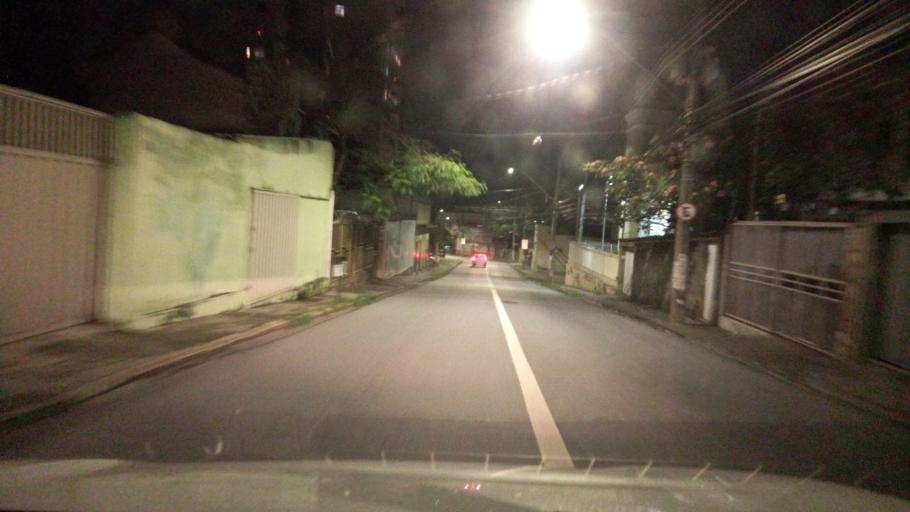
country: BR
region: Minas Gerais
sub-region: Belo Horizonte
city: Belo Horizonte
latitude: -19.9116
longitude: -43.9622
